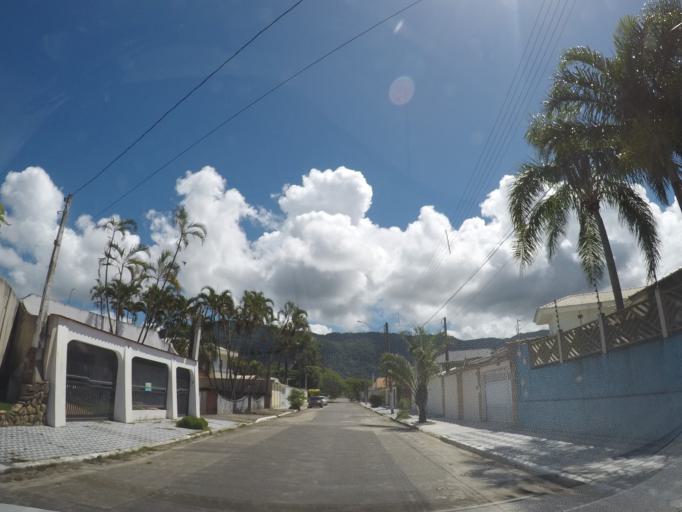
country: BR
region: Sao Paulo
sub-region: Mongagua
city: Mongagua
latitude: -24.0749
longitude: -46.5781
